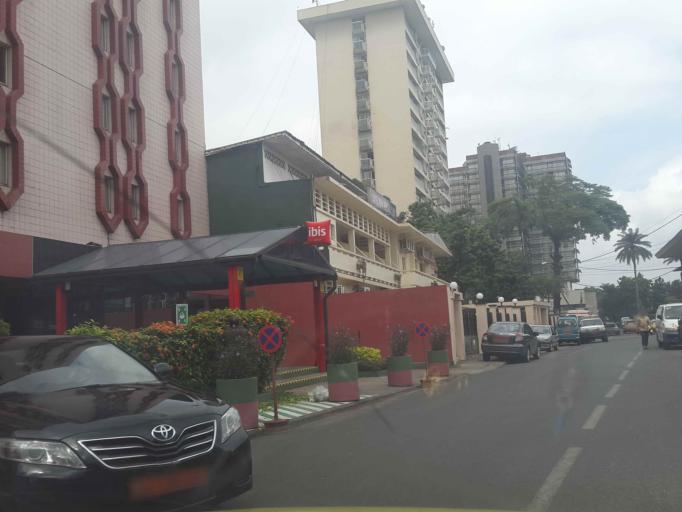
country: CM
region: Littoral
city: Douala
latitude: 4.0394
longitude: 9.6879
